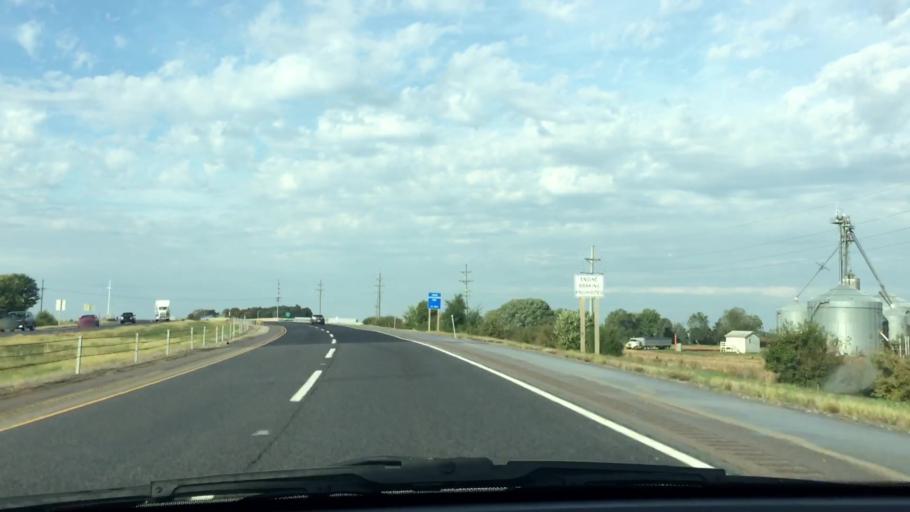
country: US
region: Illinois
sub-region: Lee County
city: Dixon
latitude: 41.8249
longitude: -89.4502
